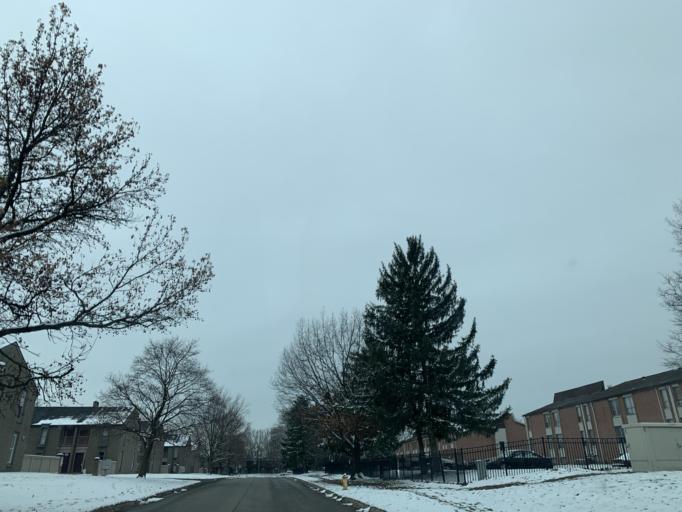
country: US
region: Ohio
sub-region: Franklin County
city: Minerva Park
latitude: 40.0572
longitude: -82.9600
